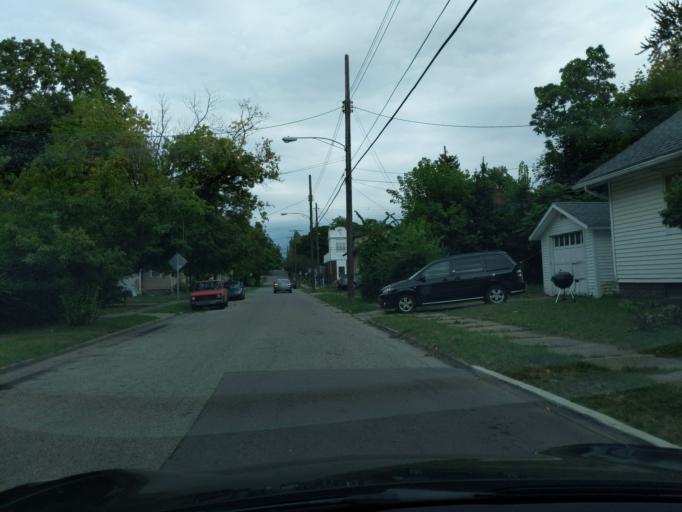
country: US
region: Michigan
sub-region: Ingham County
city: Lansing
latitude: 42.7240
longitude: -84.5317
